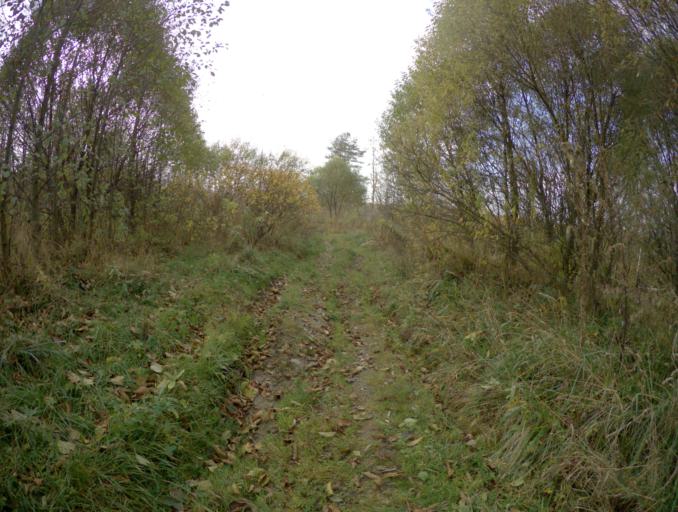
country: RU
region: Vladimir
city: Golovino
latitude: 55.9728
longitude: 40.3869
